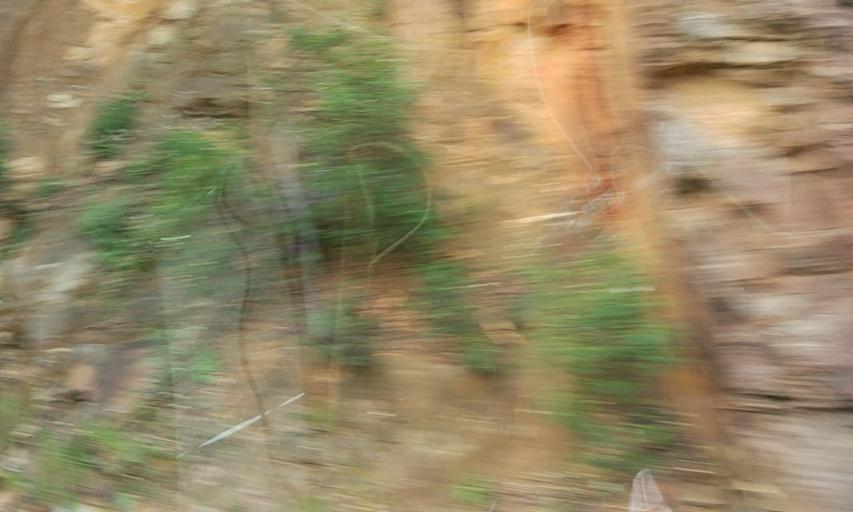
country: ES
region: Extremadura
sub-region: Provincia de Caceres
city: Acebo
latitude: 40.2010
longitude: -6.6762
